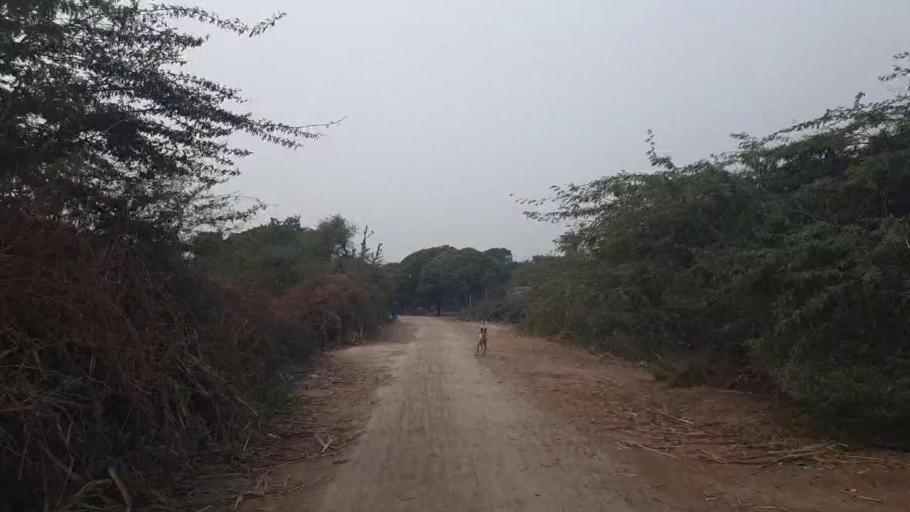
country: PK
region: Sindh
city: Tando Adam
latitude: 25.7284
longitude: 68.6820
